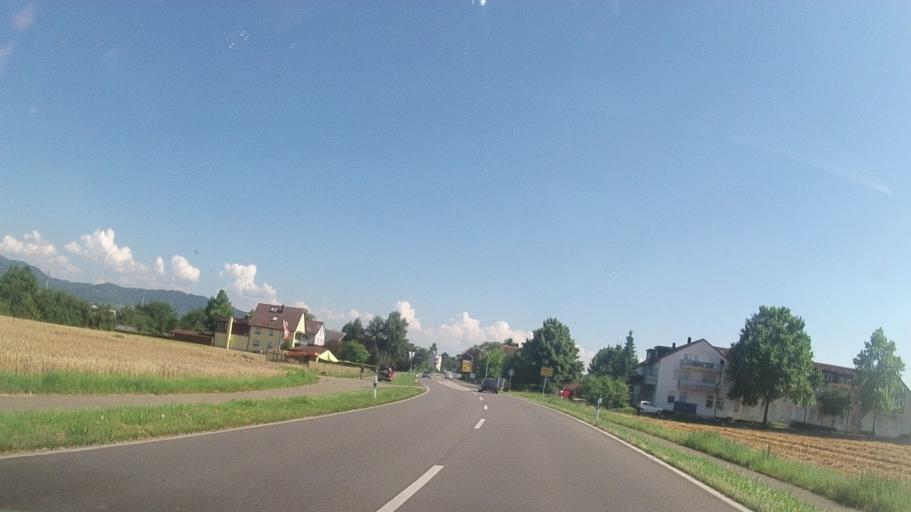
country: DE
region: Baden-Wuerttemberg
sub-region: Freiburg Region
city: Offenburg
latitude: 48.4885
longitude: 7.9366
